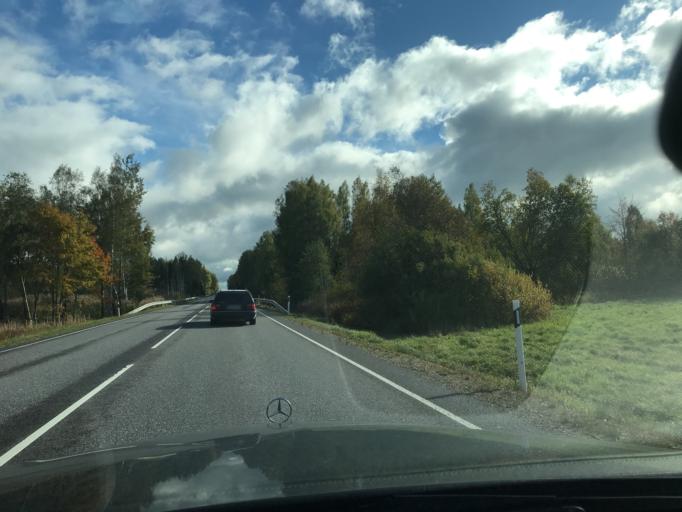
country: EE
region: Vorumaa
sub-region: Voru linn
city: Voru
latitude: 57.7778
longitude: 27.1224
